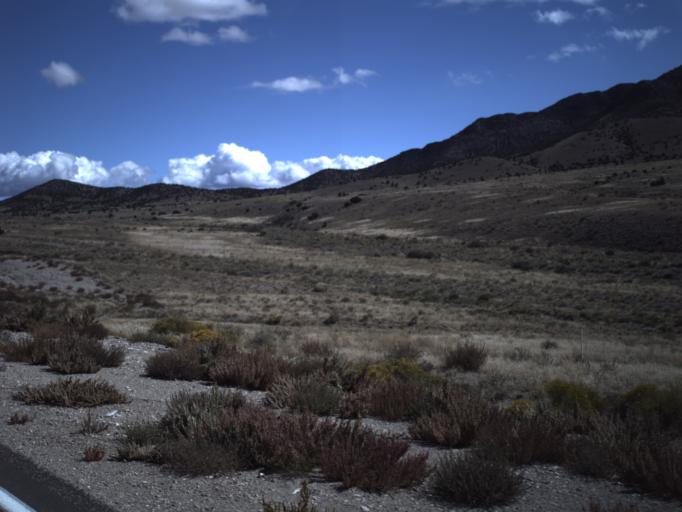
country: US
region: Utah
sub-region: Beaver County
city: Milford
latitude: 38.5124
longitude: -113.5816
